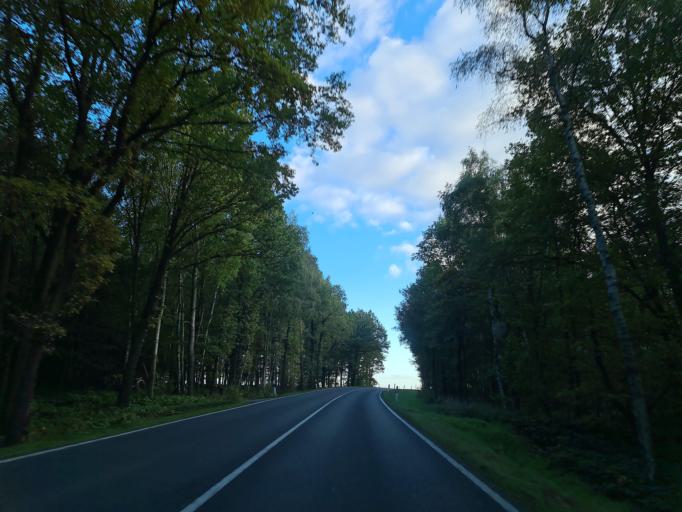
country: DE
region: Thuringia
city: Teichwitz
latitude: 50.7539
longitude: 12.0914
